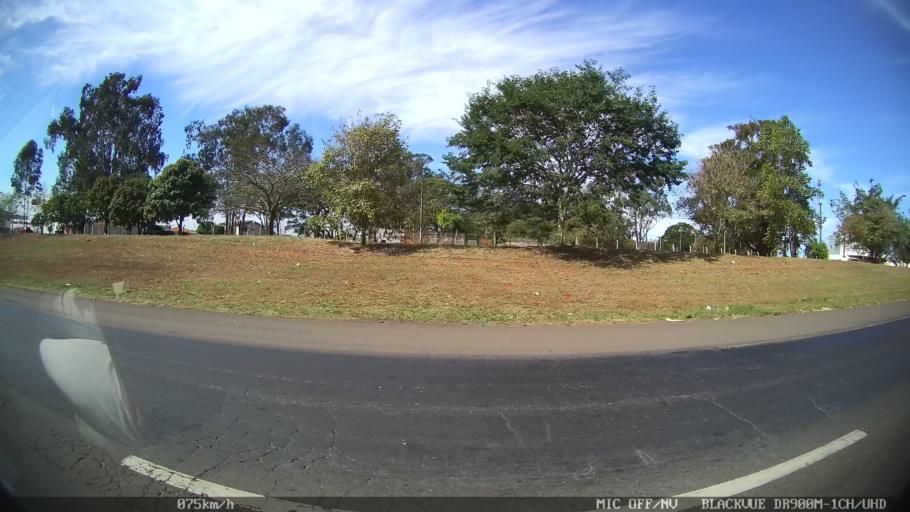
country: BR
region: Sao Paulo
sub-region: Sao Jose Do Rio Preto
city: Sao Jose do Rio Preto
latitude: -20.8206
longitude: -49.3575
